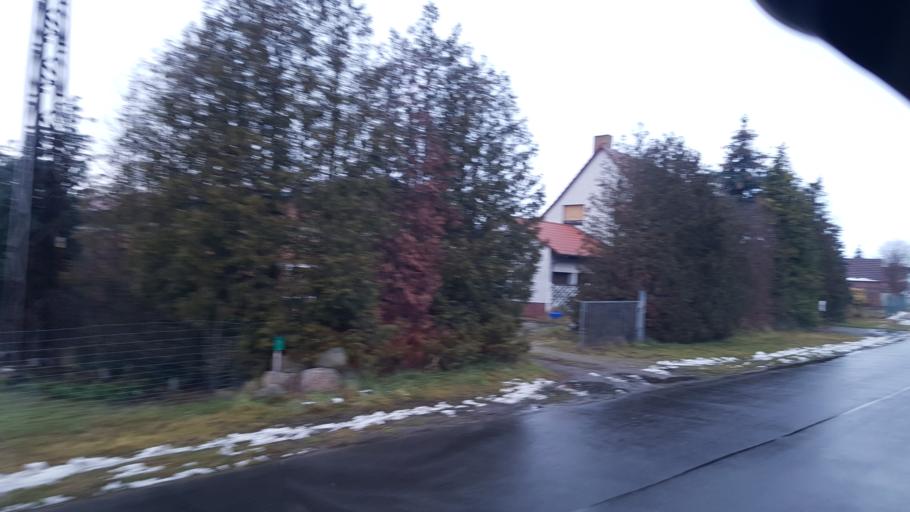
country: DE
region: Brandenburg
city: Janschwalde
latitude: 51.8631
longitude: 14.5090
